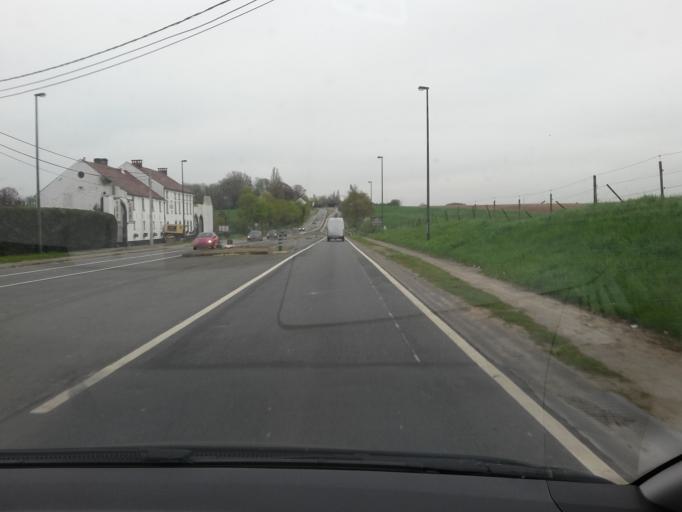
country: BE
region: Wallonia
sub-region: Province du Brabant Wallon
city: Genappe
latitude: 50.6503
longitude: 4.4167
